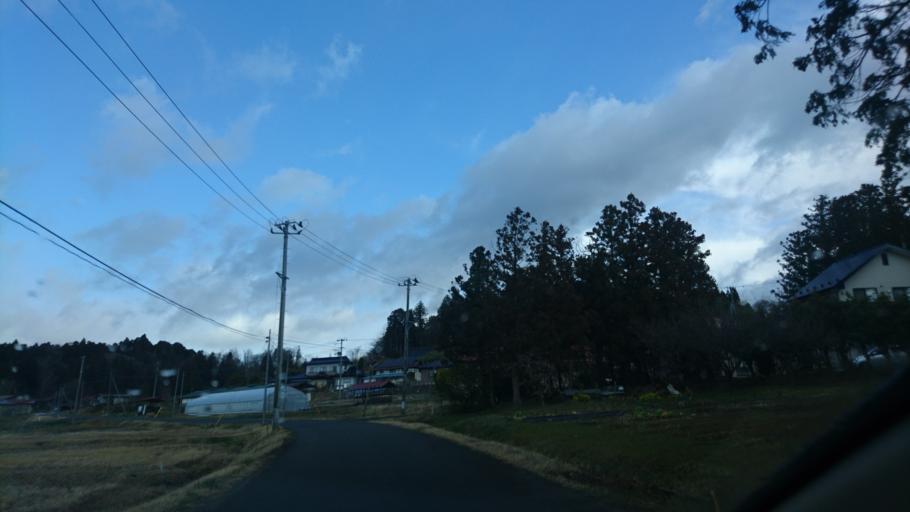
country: JP
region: Iwate
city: Ichinoseki
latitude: 38.7924
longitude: 141.0307
